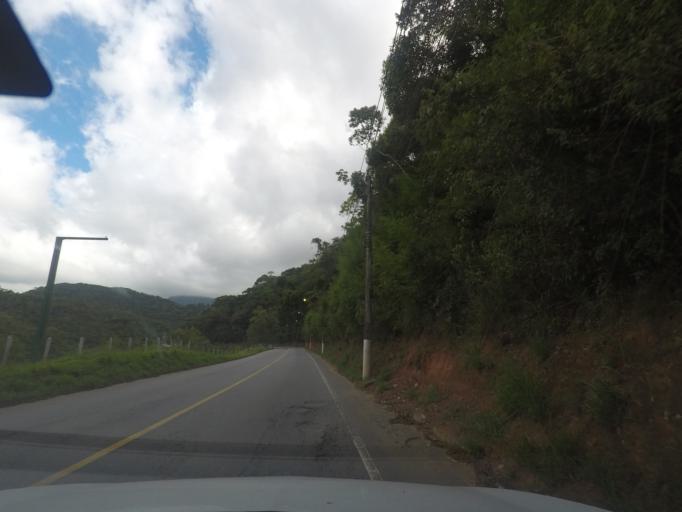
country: BR
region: Rio de Janeiro
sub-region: Teresopolis
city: Teresopolis
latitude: -22.3935
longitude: -42.9570
